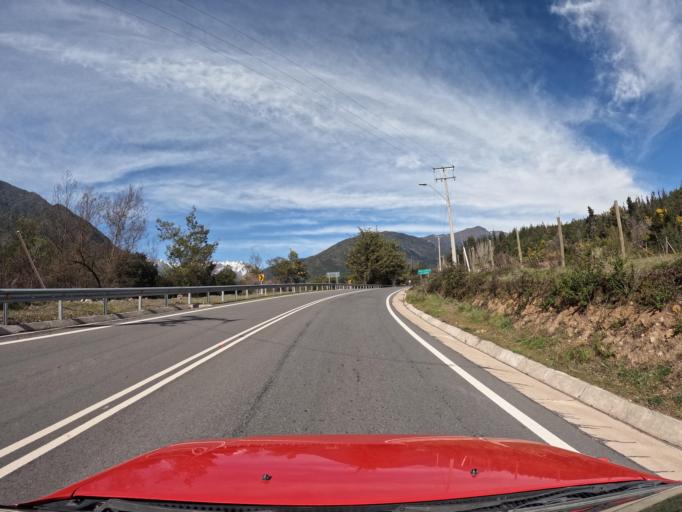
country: CL
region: O'Higgins
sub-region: Provincia de Colchagua
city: Chimbarongo
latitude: -34.9984
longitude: -70.8183
